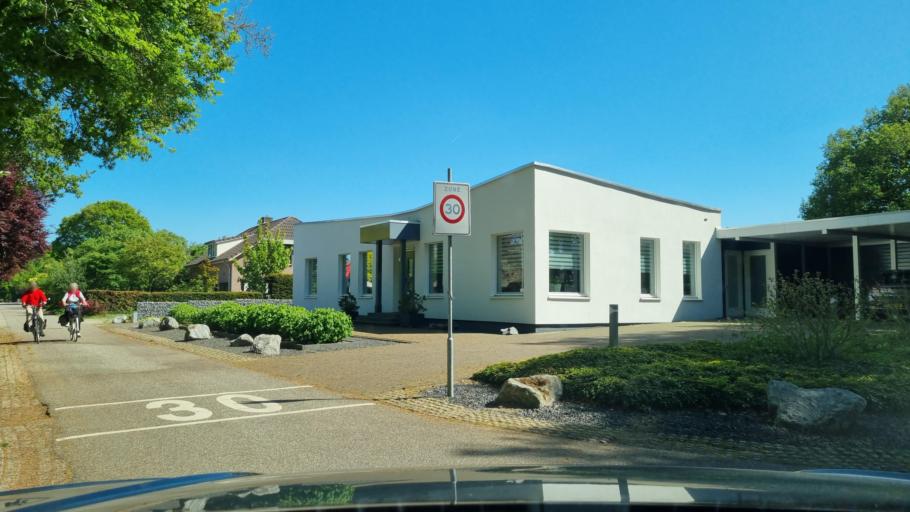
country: NL
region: North Brabant
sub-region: Gemeente Cuijk
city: Cuijk
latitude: 51.7378
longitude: 5.9074
